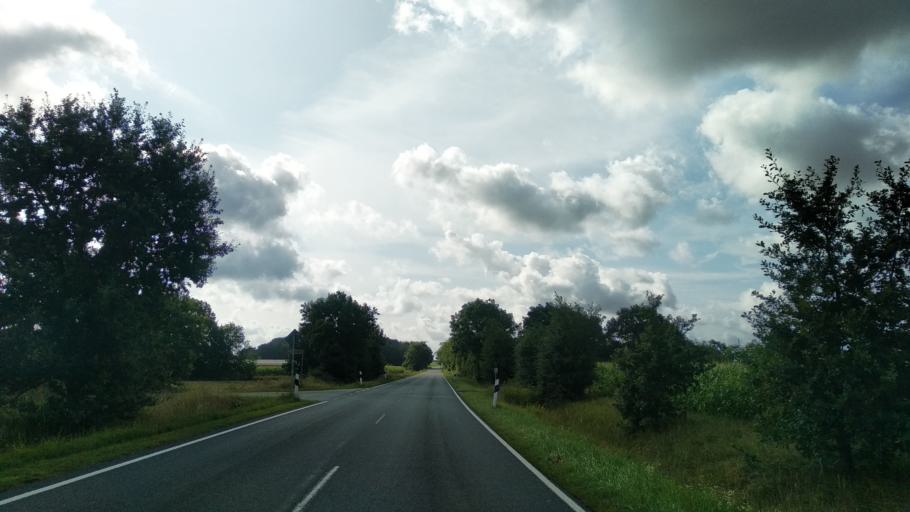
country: DE
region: Schleswig-Holstein
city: Lottorf
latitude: 54.4568
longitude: 9.5863
